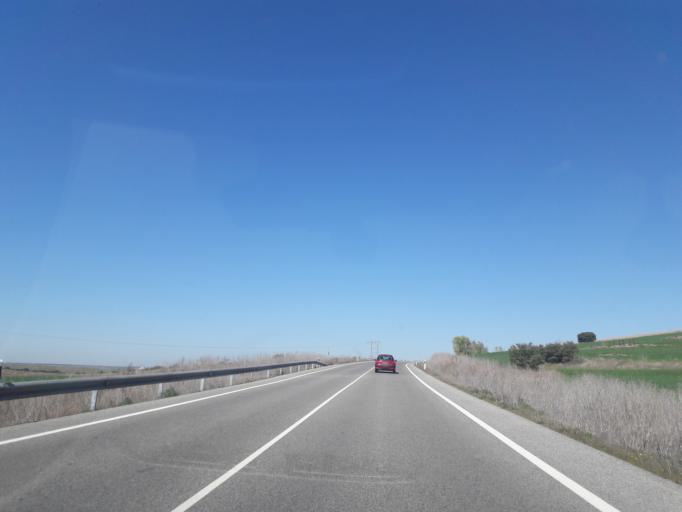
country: ES
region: Castille and Leon
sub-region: Provincia de Salamanca
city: Arapiles
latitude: 40.8813
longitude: -5.6614
